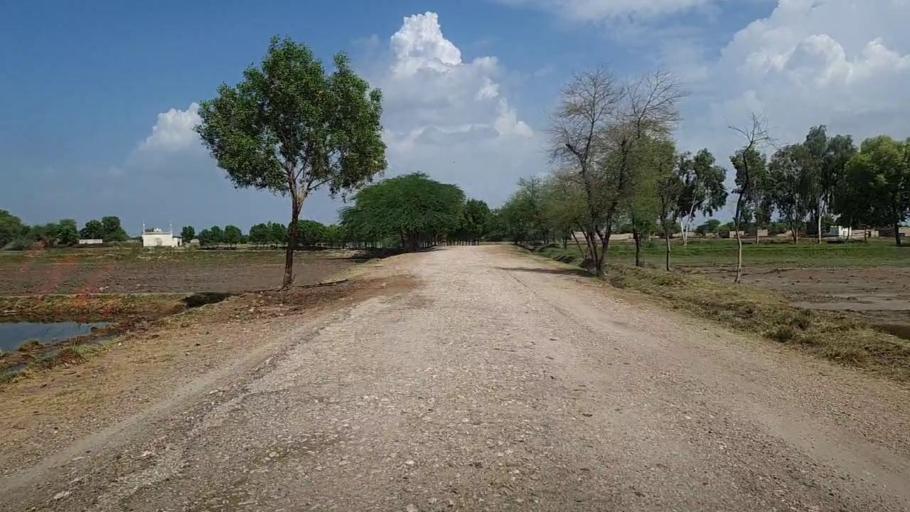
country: PK
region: Sindh
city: Bhiria
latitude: 26.9186
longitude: 68.2298
